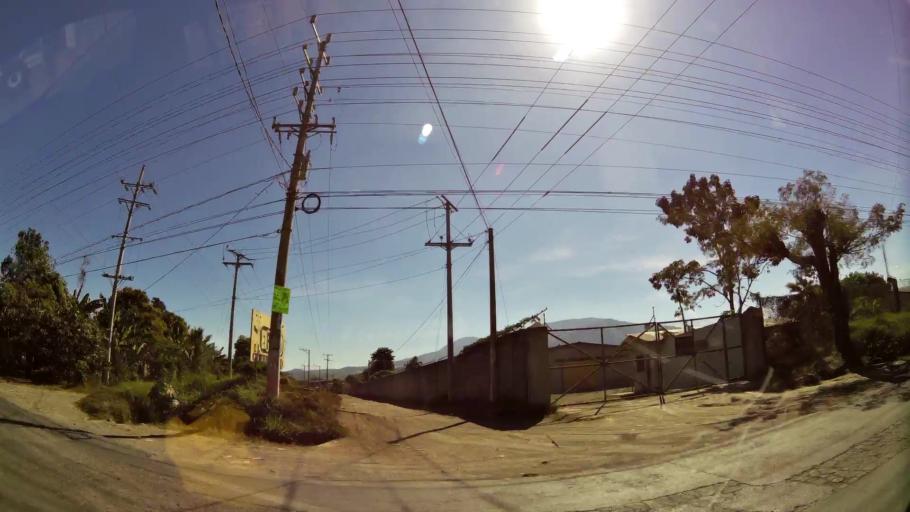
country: SV
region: La Libertad
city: San Juan Opico
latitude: 13.7990
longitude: -89.3652
